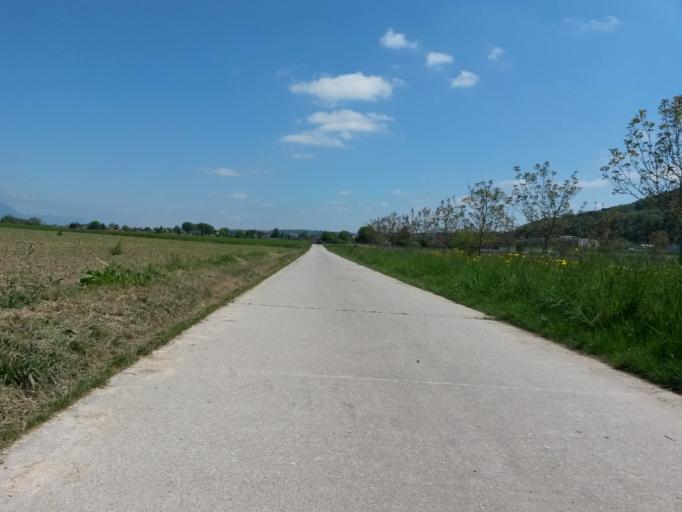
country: CH
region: Bern
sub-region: Biel/Bienne District
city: Meinisberg
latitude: 47.1377
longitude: 7.3543
